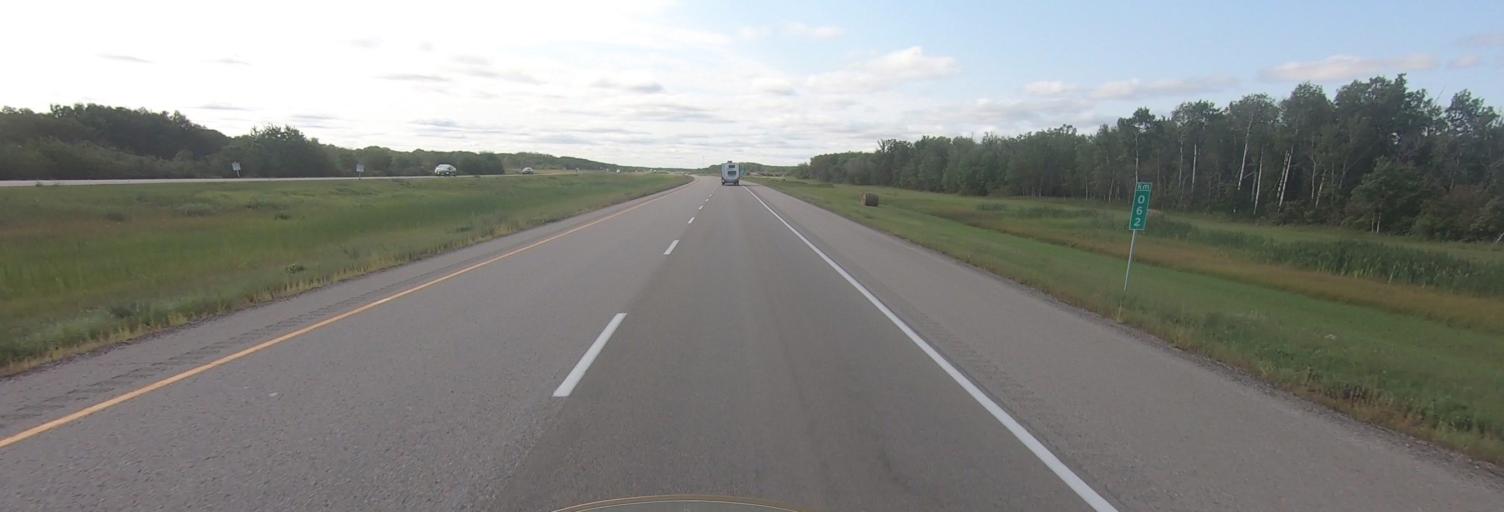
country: CA
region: Manitoba
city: Virden
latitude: 49.7744
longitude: -100.7280
